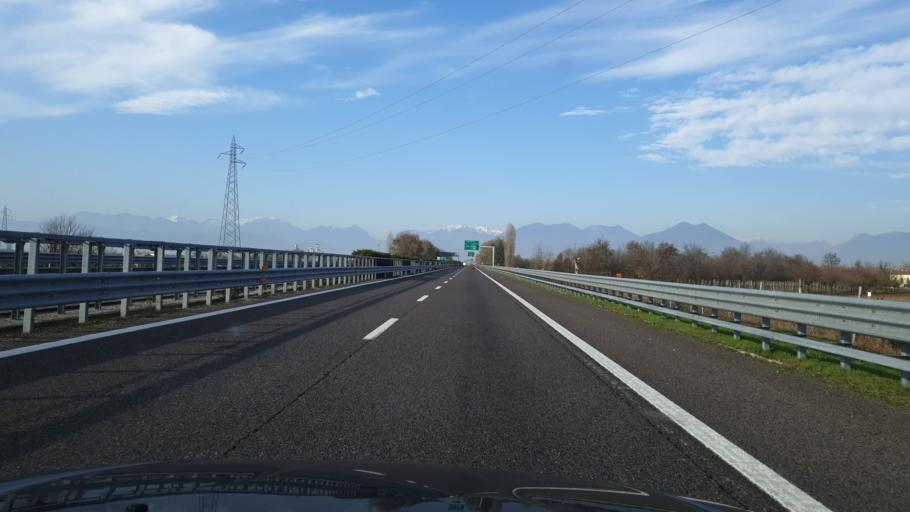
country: IT
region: Veneto
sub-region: Provincia di Vicenza
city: Novoledo
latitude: 45.6554
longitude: 11.5339
